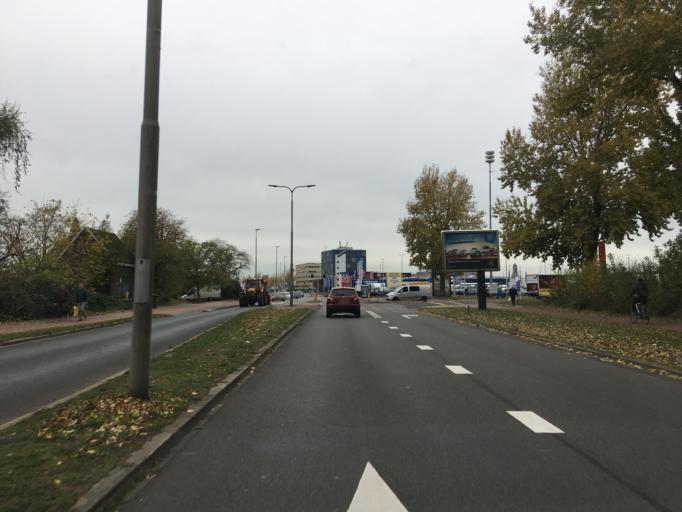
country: NL
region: Gelderland
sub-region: Gemeente Arnhem
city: Arnhem
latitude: 51.9714
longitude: 5.9364
